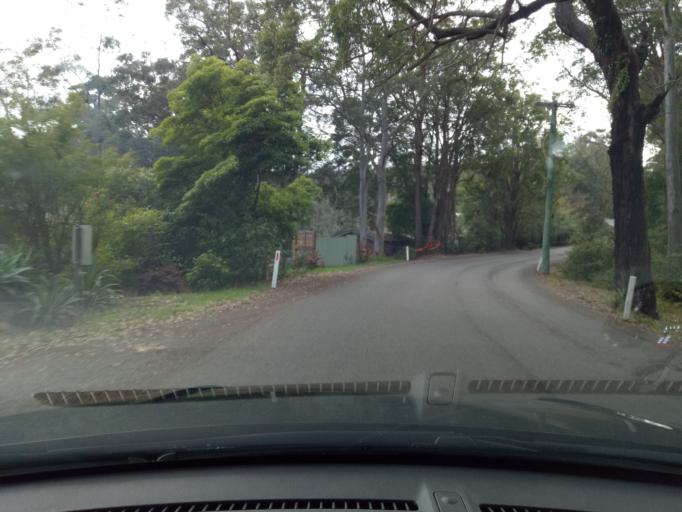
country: AU
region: New South Wales
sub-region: Gosford Shire
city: Holgate
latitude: -33.3842
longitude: 151.4106
